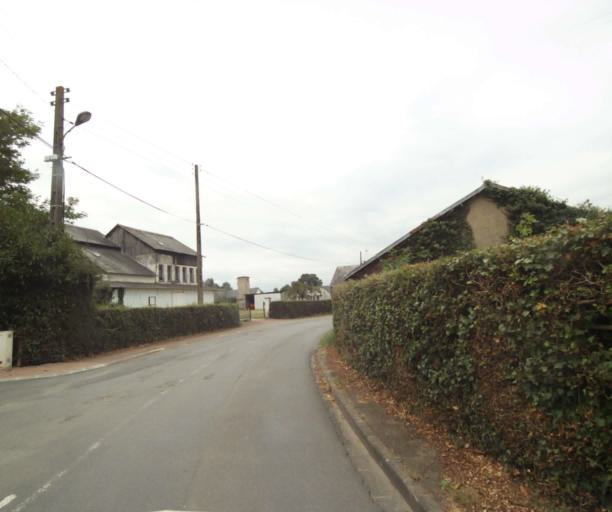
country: FR
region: Pays de la Loire
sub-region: Departement de la Sarthe
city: Sable-sur-Sarthe
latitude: 47.8313
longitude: -0.3252
